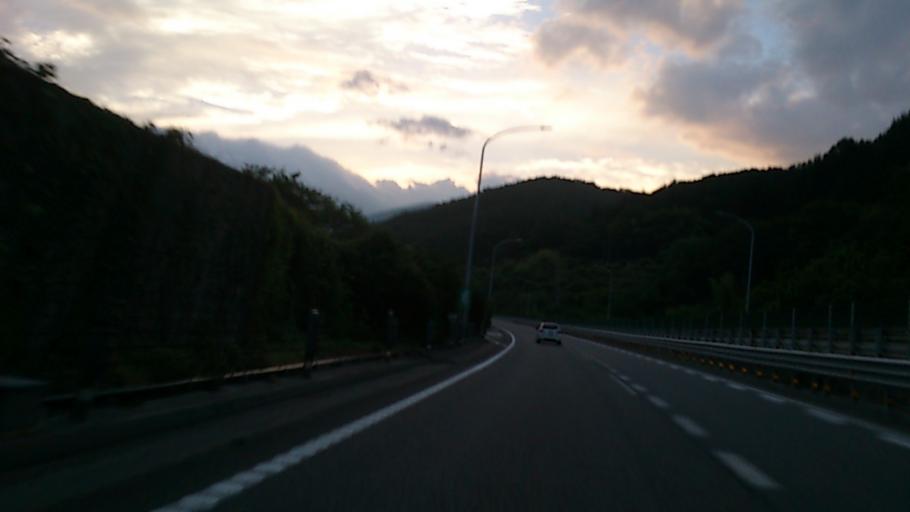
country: JP
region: Nagano
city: Iida
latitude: 35.4478
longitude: 137.7361
